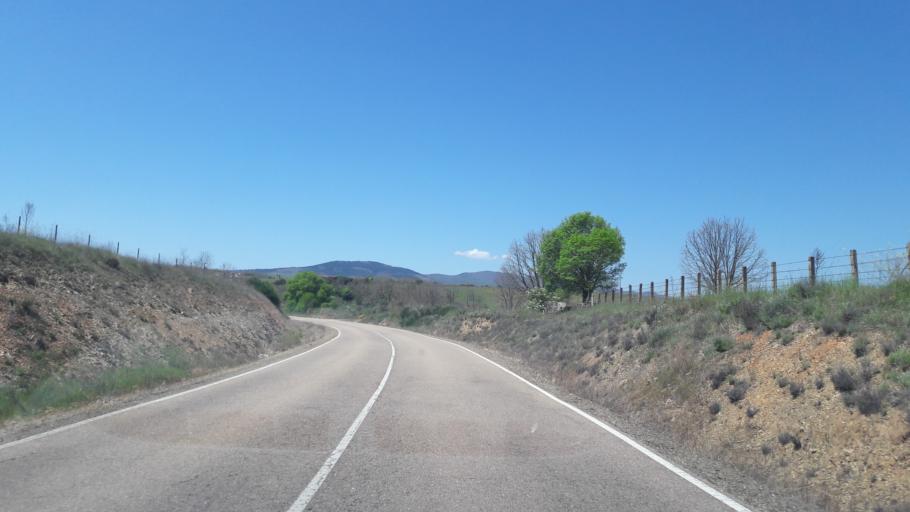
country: ES
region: Castille and Leon
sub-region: Provincia de Salamanca
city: Monleon
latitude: 40.5909
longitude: -5.8329
